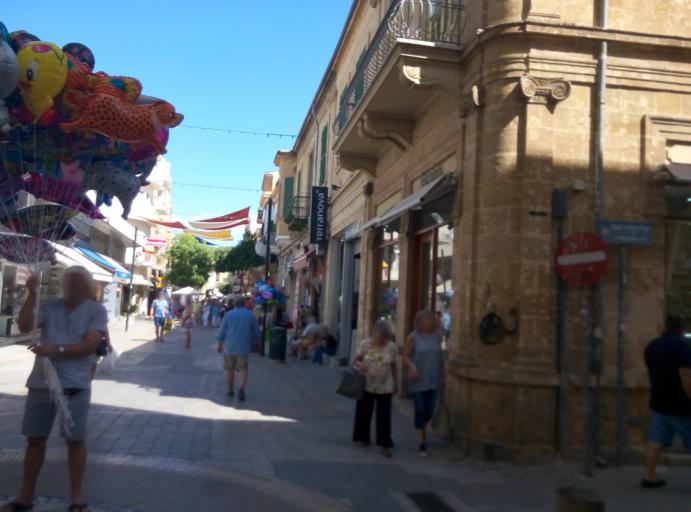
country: CY
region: Lefkosia
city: Nicosia
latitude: 35.1724
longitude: 33.3613
